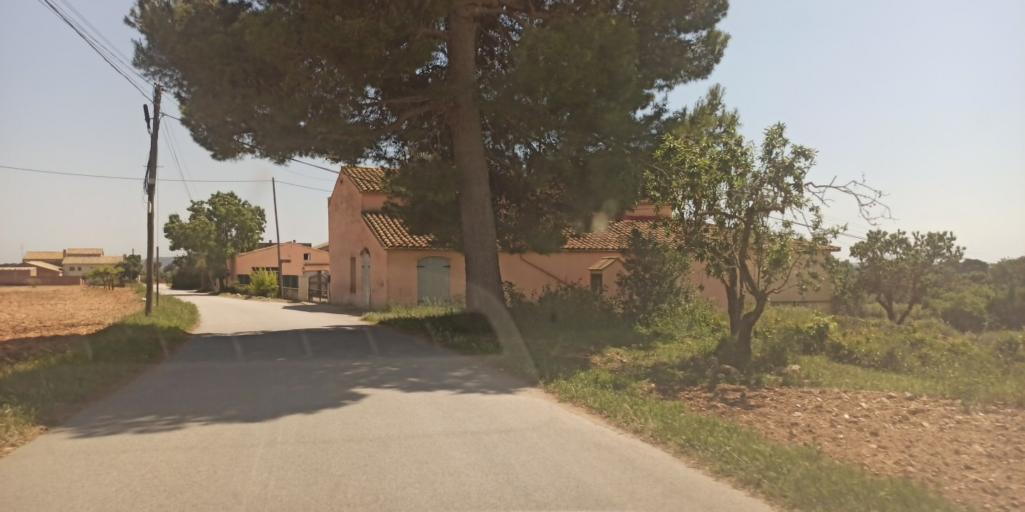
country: ES
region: Catalonia
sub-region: Provincia de Barcelona
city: Vilobi del Penedes
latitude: 41.3644
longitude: 1.6400
